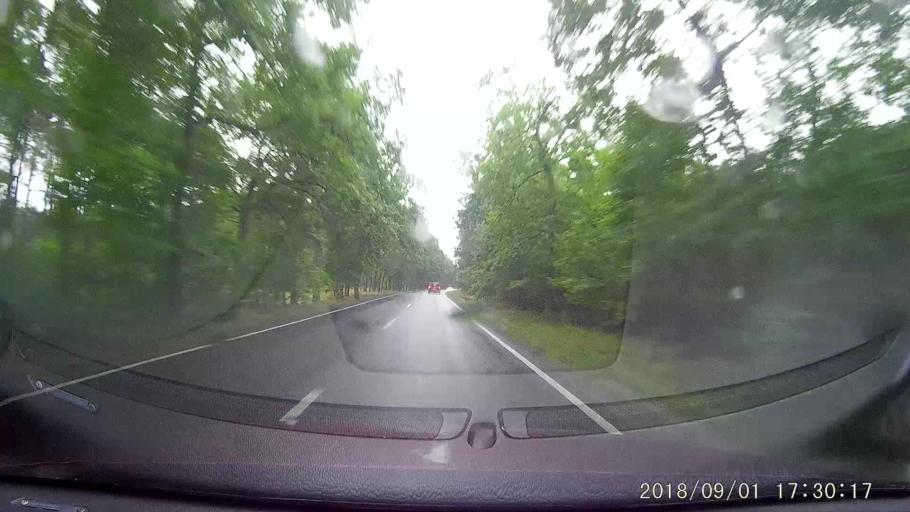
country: PL
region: Lubusz
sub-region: Powiat zaganski
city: Zagan
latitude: 51.6436
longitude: 15.3191
